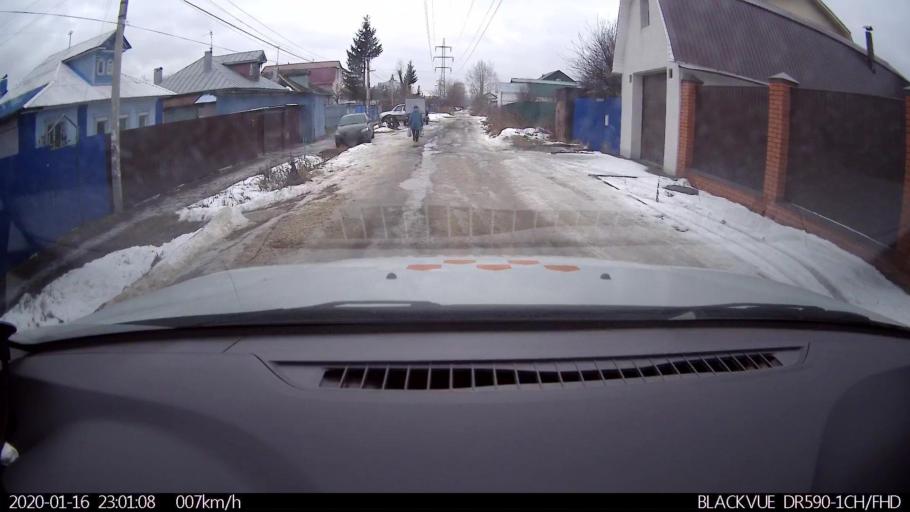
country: RU
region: Nizjnij Novgorod
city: Nizhniy Novgorod
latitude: 56.2852
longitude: 43.9051
